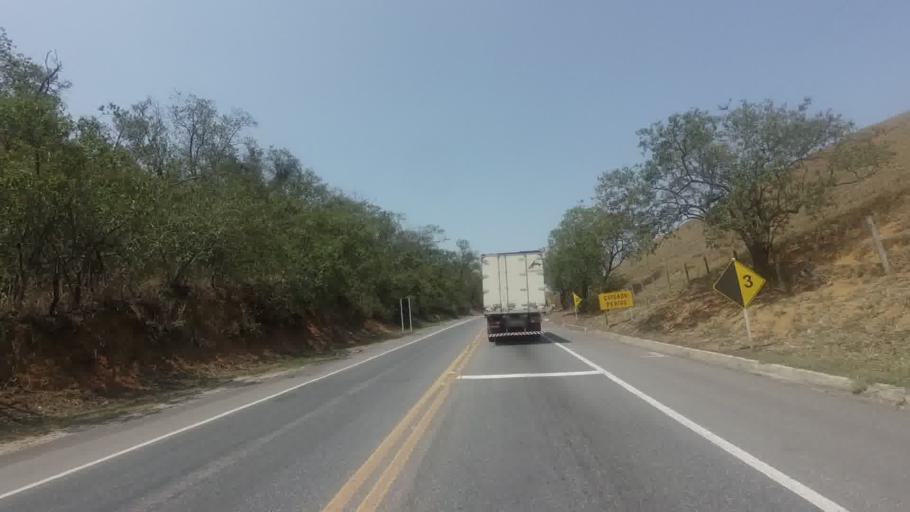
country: BR
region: Espirito Santo
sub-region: Rio Novo Do Sul
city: Rio Novo do Sul
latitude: -20.8588
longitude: -40.8762
